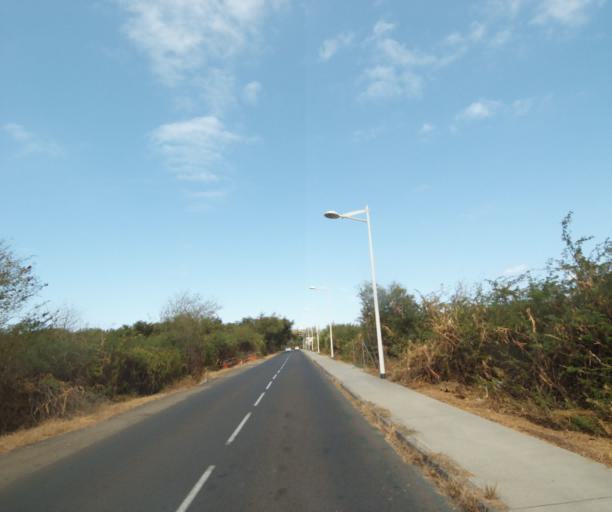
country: RE
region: Reunion
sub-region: Reunion
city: Trois-Bassins
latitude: -21.0841
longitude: 55.2339
